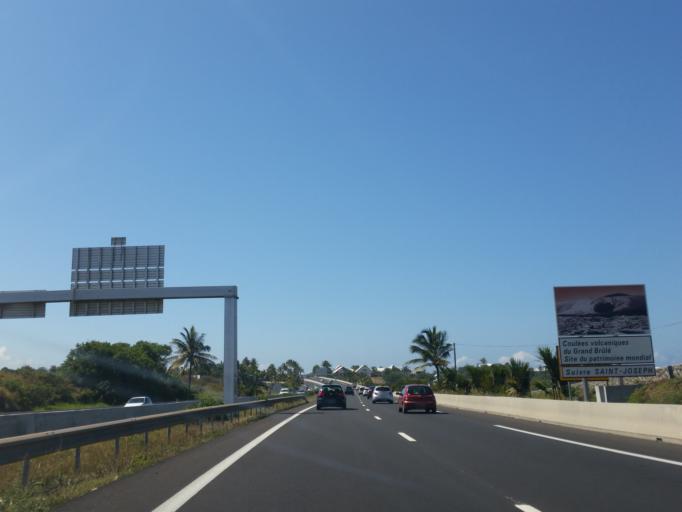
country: RE
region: Reunion
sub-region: Reunion
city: Saint-Pierre
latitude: -21.3282
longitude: 55.4518
